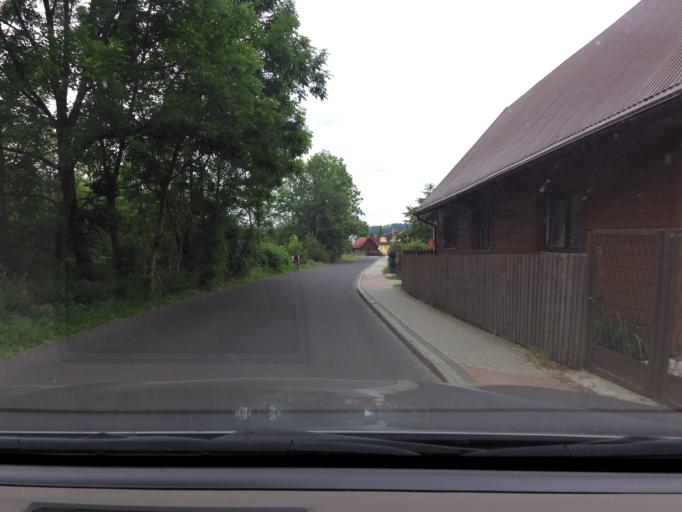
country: PL
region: Silesian Voivodeship
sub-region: Powiat zywiecki
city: Ujsoly
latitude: 49.4732
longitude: 19.1495
